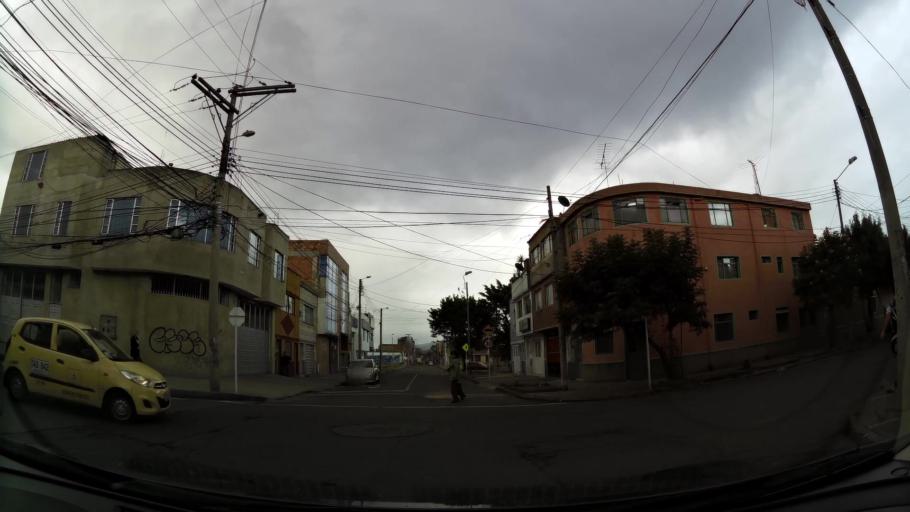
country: CO
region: Bogota D.C.
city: Barrio San Luis
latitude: 4.6660
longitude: -74.0767
